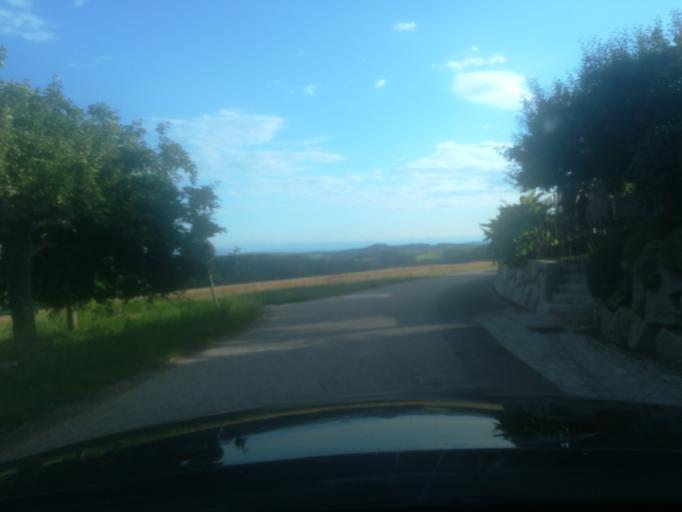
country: AT
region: Upper Austria
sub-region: Politischer Bezirk Perg
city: Perg
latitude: 48.3519
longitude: 14.5697
